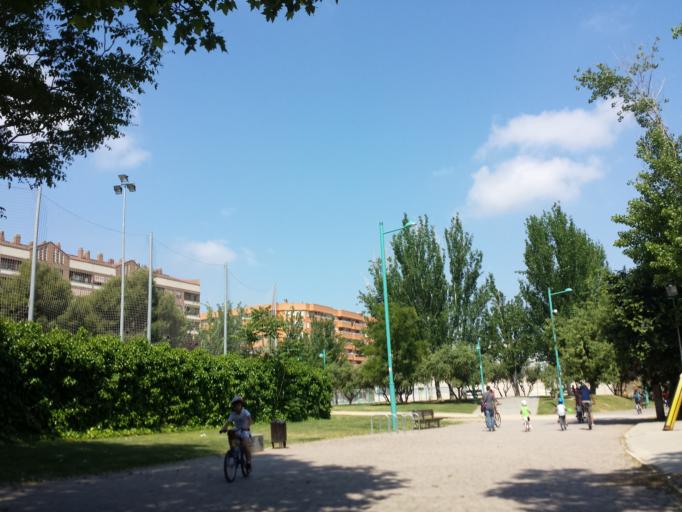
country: ES
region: Aragon
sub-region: Provincia de Zaragoza
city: Almozara
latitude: 41.6622
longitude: -0.8941
